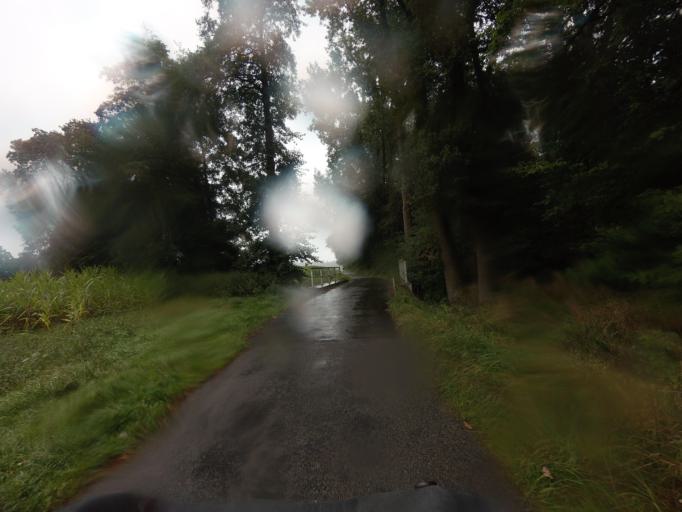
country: DE
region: North Rhine-Westphalia
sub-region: Regierungsbezirk Munster
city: Gronau
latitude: 52.1871
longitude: 6.9798
